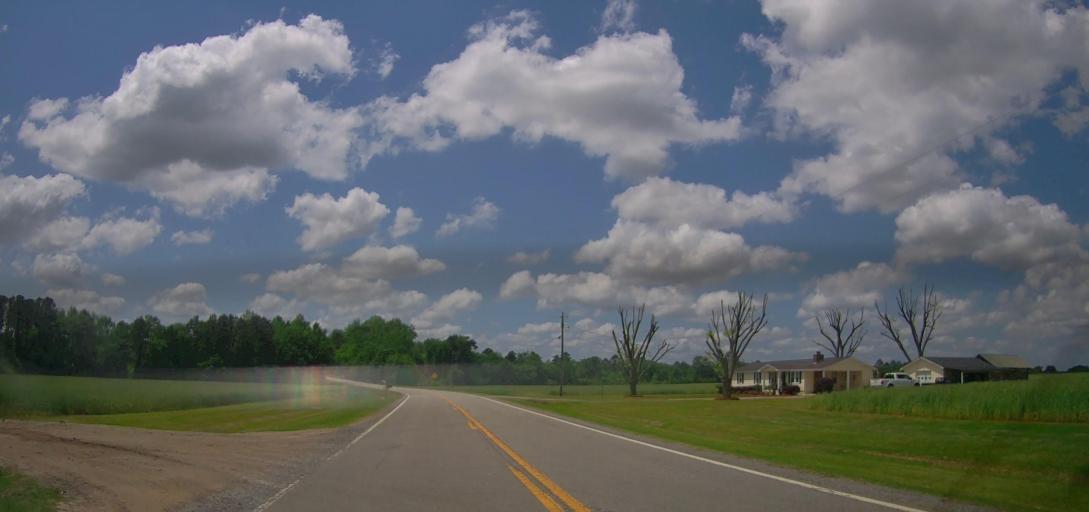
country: US
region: Georgia
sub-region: Dodge County
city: Chester
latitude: 32.5556
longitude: -83.1746
